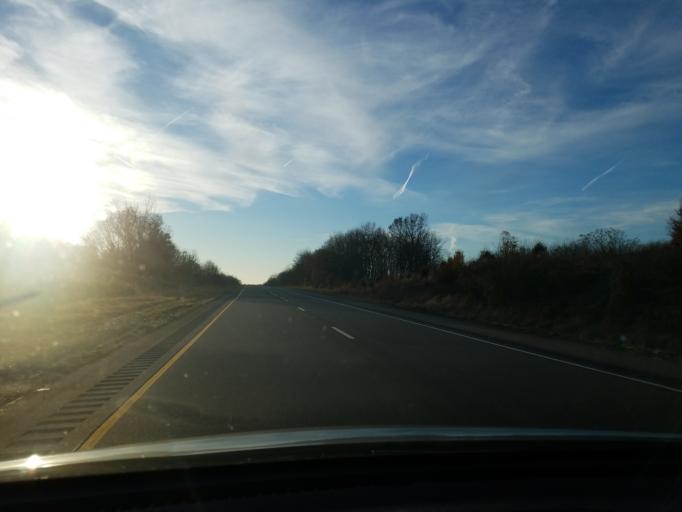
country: US
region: Indiana
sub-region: Spencer County
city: Dale
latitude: 38.1989
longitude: -87.1242
